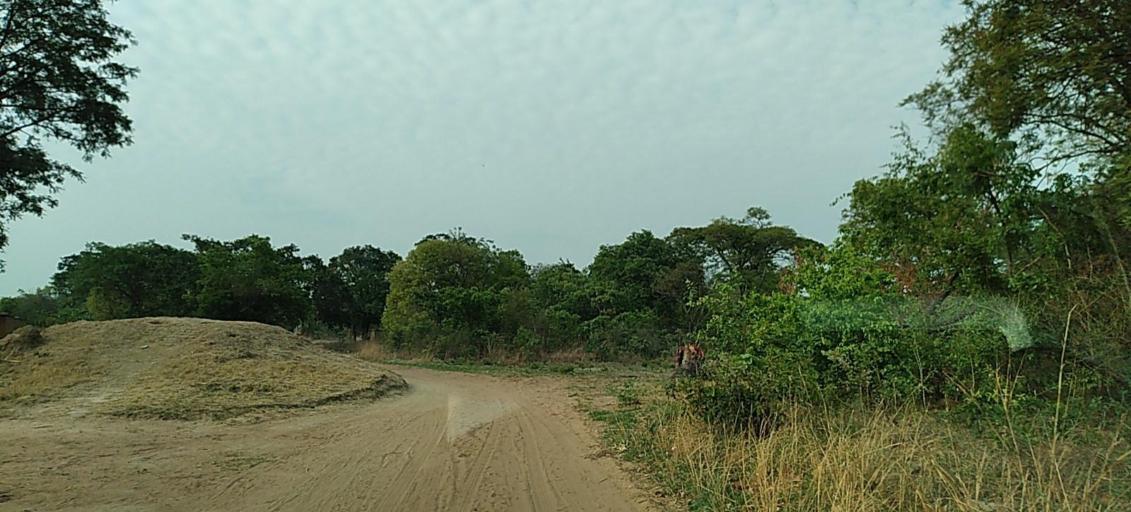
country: ZM
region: Copperbelt
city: Kalulushi
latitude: -12.9110
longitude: 27.6890
